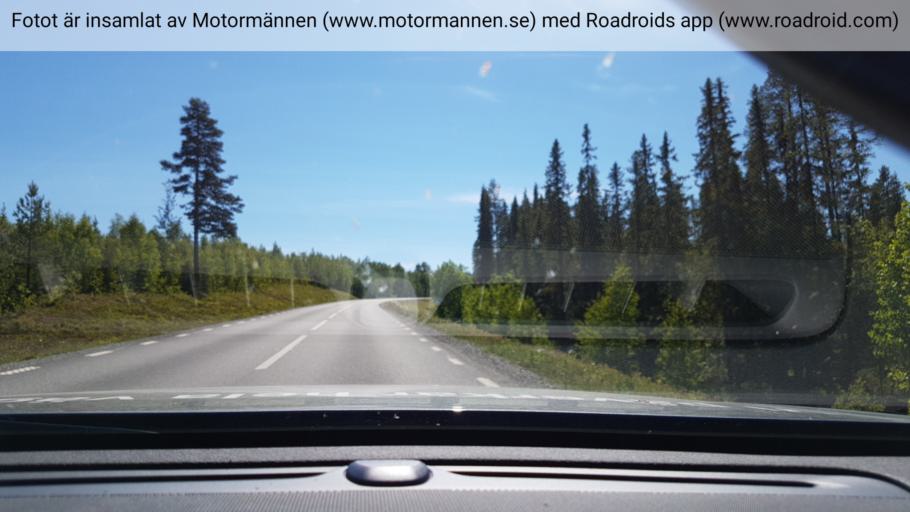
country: SE
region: Vaesterbotten
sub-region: Vilhelmina Kommun
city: Vilhelmina
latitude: 64.6821
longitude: 16.7285
